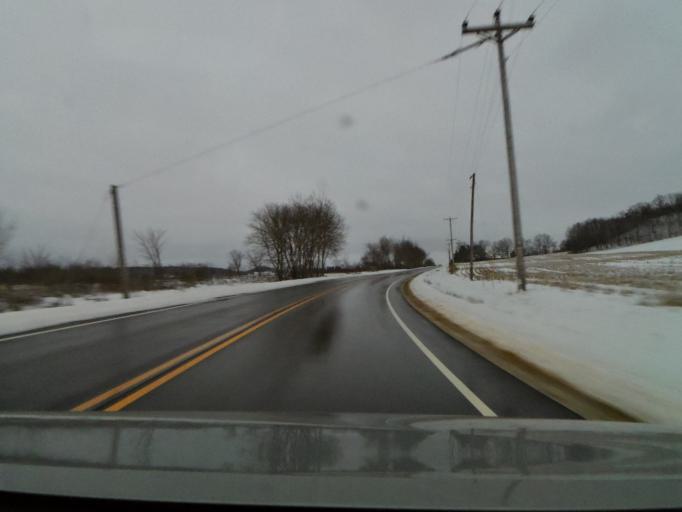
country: US
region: Wisconsin
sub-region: Dunn County
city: Boyceville
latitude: 44.9554
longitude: -92.0598
